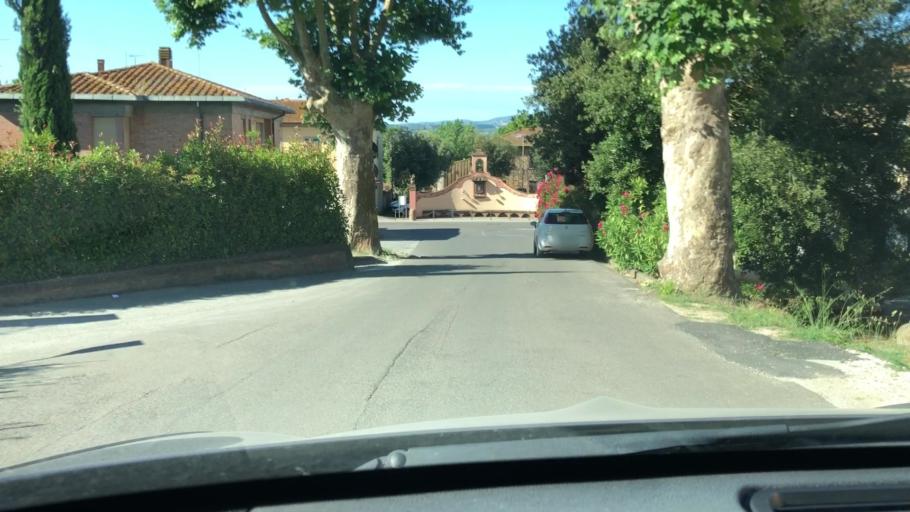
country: IT
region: Tuscany
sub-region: Province of Pisa
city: Forcoli
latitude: 43.6046
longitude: 10.7043
